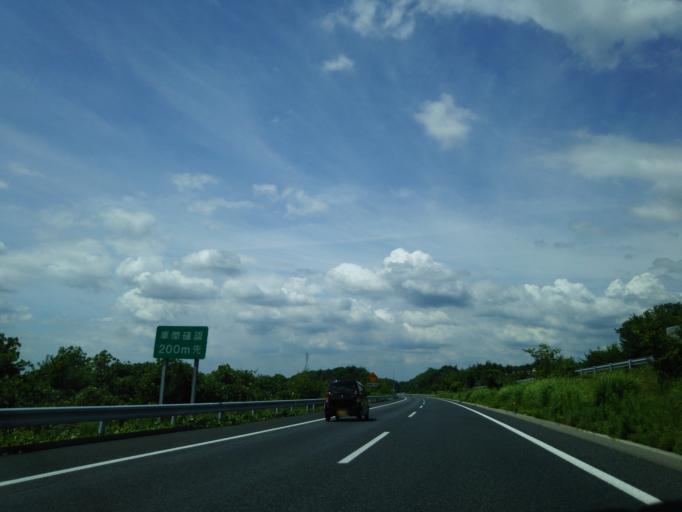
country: JP
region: Gifu
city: Toki
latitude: 35.3055
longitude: 137.1801
